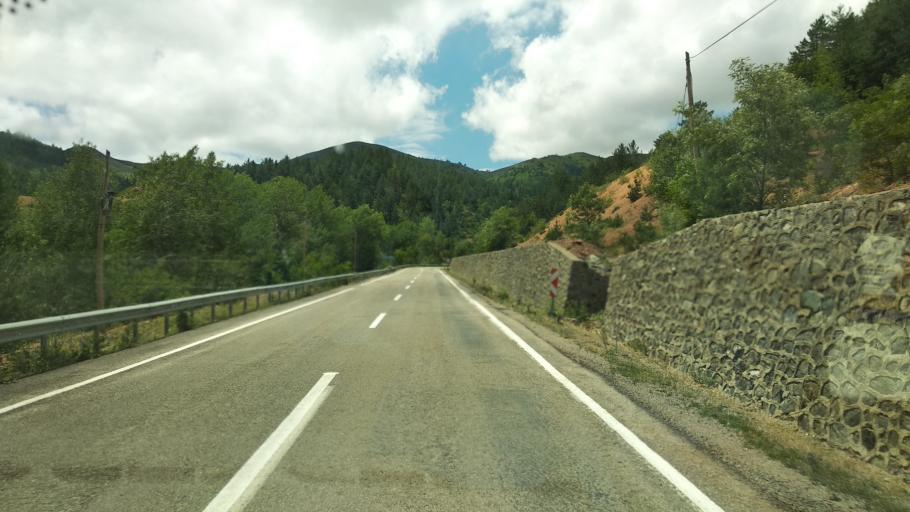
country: TR
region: Gumushane
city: Kose
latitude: 40.3031
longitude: 39.5564
